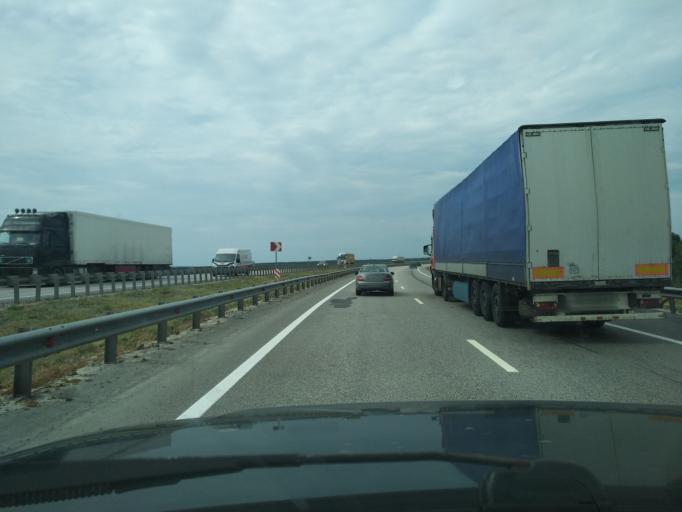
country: RU
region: Lipetsk
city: Khlevnoye
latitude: 52.0635
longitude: 39.1804
